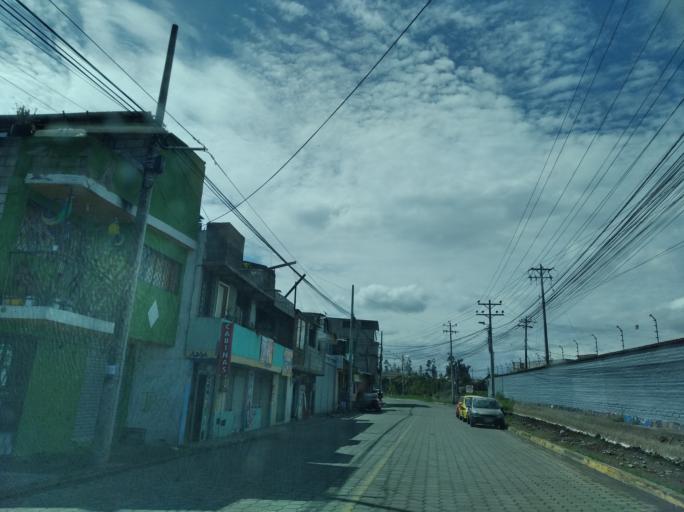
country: EC
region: Pichincha
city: Sangolqui
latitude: -0.2164
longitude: -78.3397
